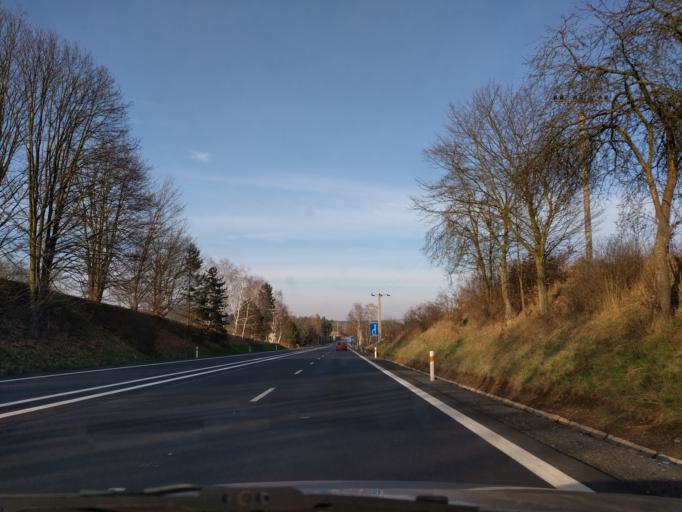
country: CZ
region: Central Bohemia
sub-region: Okres Benesov
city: Cercany
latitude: 49.8583
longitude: 14.6929
